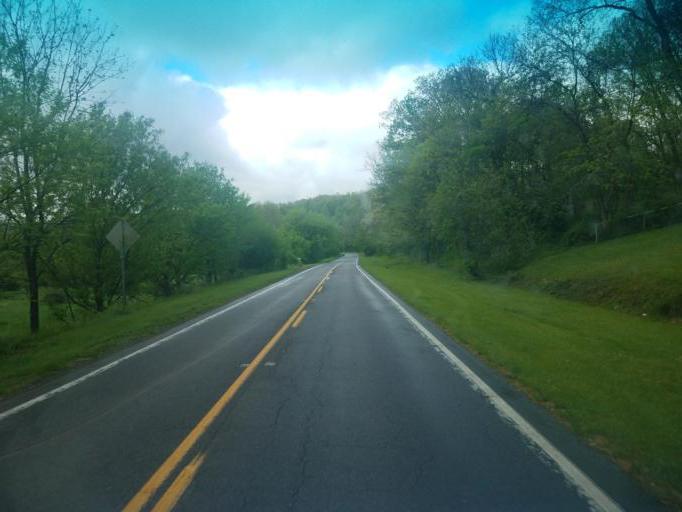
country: US
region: Virginia
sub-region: Washington County
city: Emory
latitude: 36.6660
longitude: -81.8043
